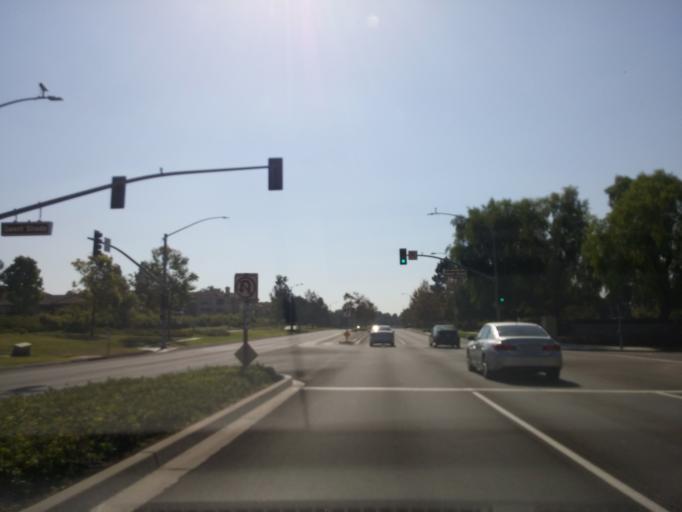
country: US
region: California
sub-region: Orange County
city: Irvine
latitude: 33.6910
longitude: -117.8160
